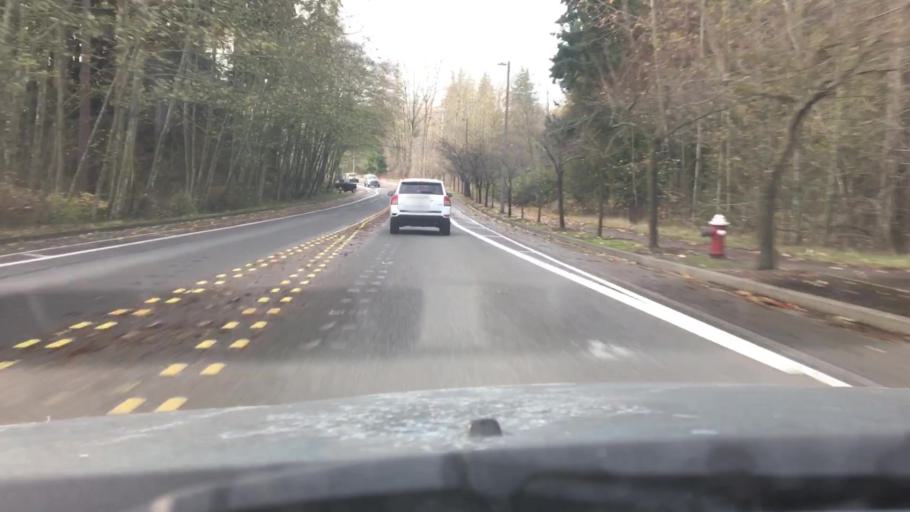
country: US
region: Washington
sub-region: Whatcom County
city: Geneva
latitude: 48.7749
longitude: -122.4329
